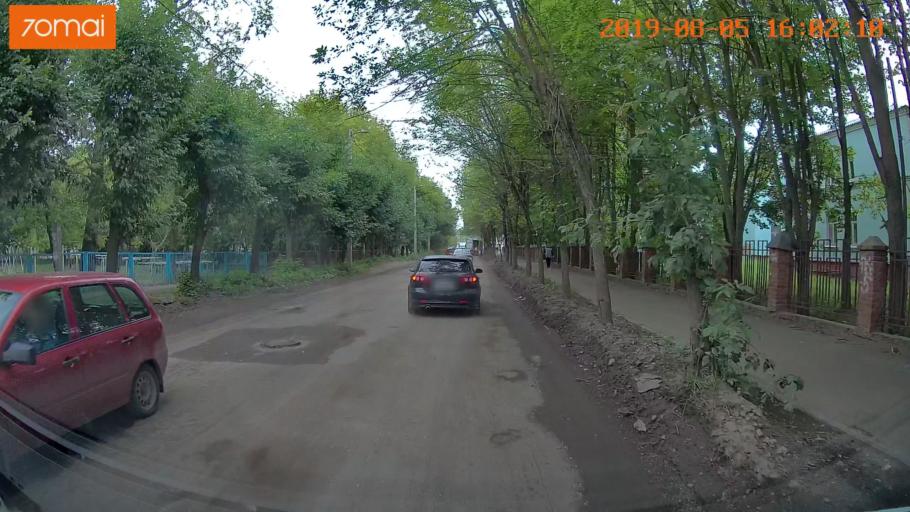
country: RU
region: Ivanovo
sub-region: Gorod Ivanovo
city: Ivanovo
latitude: 56.9771
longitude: 40.9619
